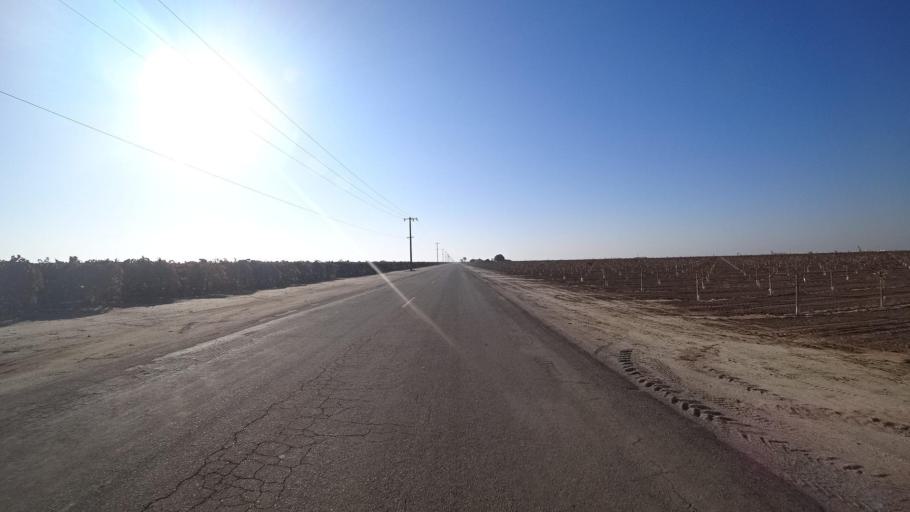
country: US
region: California
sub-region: Kern County
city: McFarland
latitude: 35.7322
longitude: -119.1695
